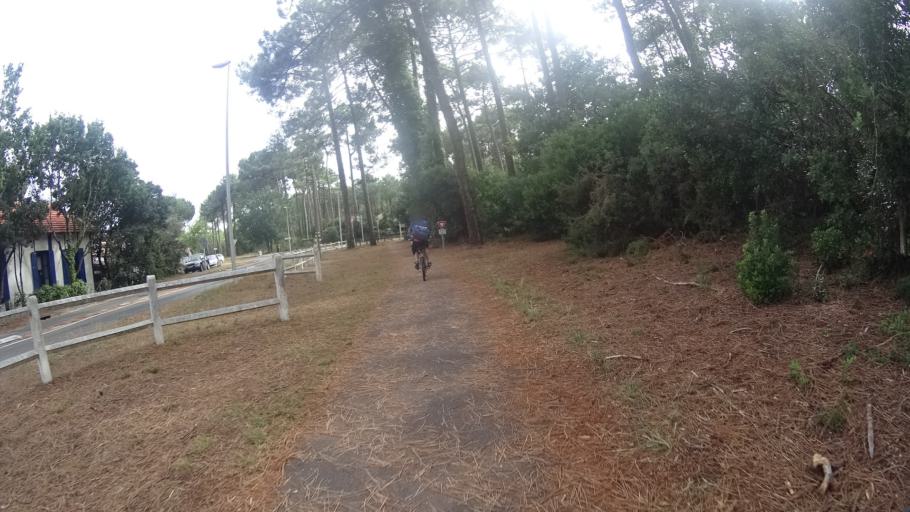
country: FR
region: Aquitaine
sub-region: Departement de la Gironde
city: Lacanau
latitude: 44.9932
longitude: -1.1466
